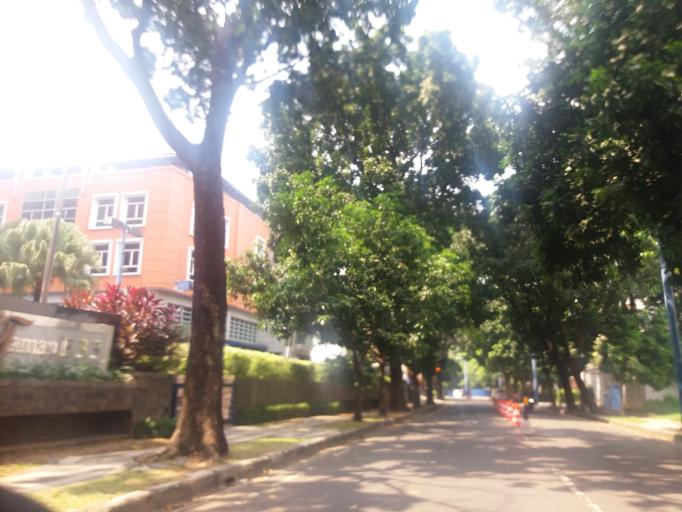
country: ID
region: Jakarta Raya
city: Jakarta
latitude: -6.2317
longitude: 106.8271
